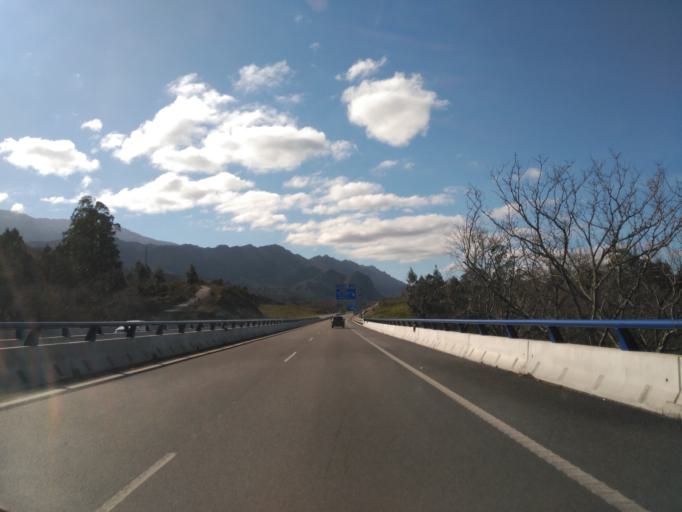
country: ES
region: Asturias
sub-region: Province of Asturias
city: Llanes
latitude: 43.4010
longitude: -4.6991
